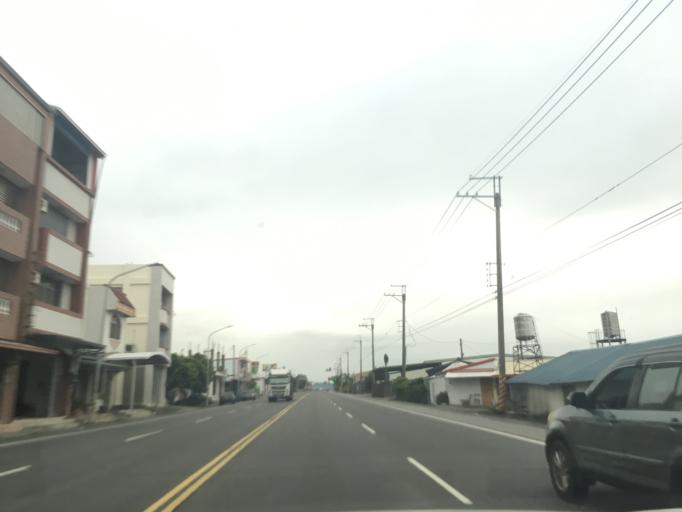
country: TW
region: Taiwan
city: Taitung City
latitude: 22.6854
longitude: 121.0438
